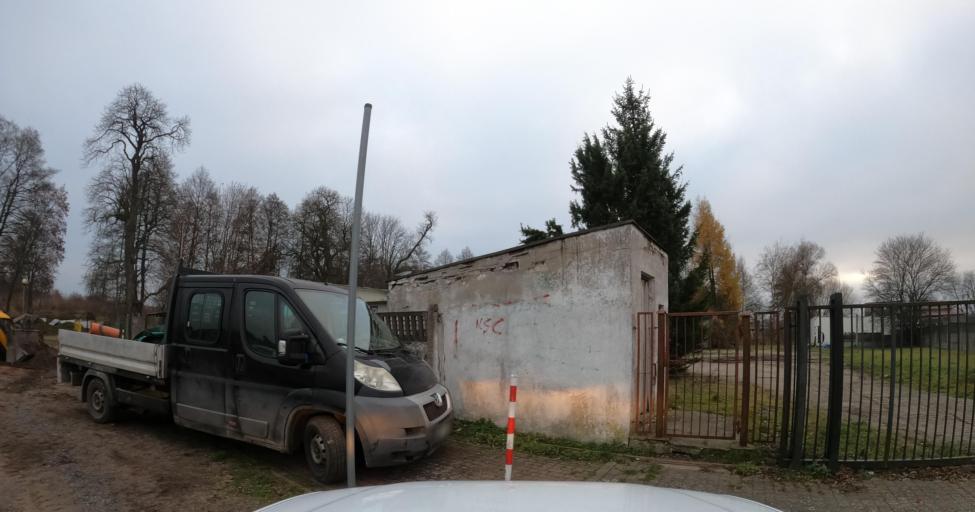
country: PL
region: West Pomeranian Voivodeship
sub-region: Powiat walecki
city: Miroslawiec
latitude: 53.3403
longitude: 16.0943
